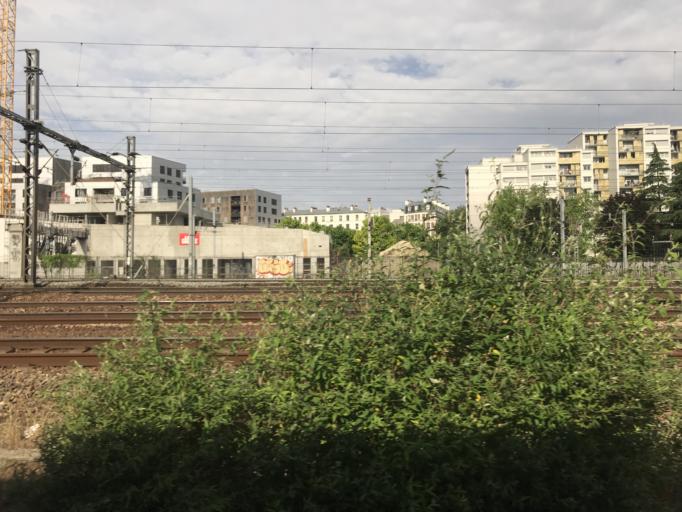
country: FR
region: Ile-de-France
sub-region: Paris
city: Saint-Ouen
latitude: 48.8951
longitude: 2.3551
